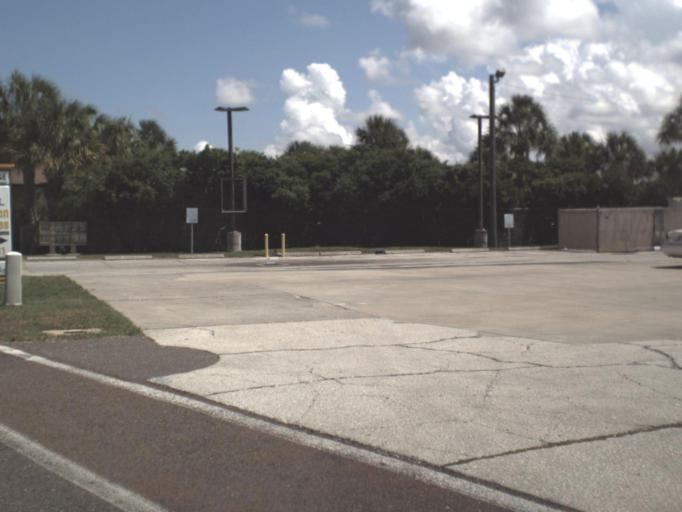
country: US
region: Florida
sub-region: Pinellas County
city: Indian Shores
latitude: 27.8533
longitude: -82.8454
